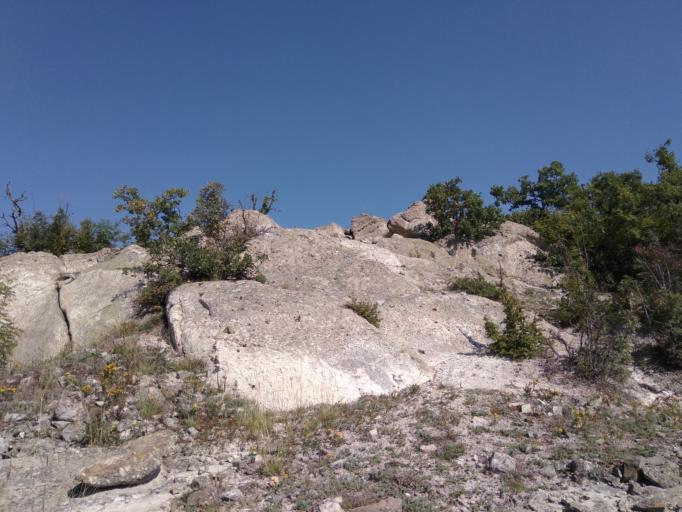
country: BG
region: Kurdzhali
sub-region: Obshtina Krumovgrad
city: Krumovgrad
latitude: 41.5141
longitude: 25.6648
